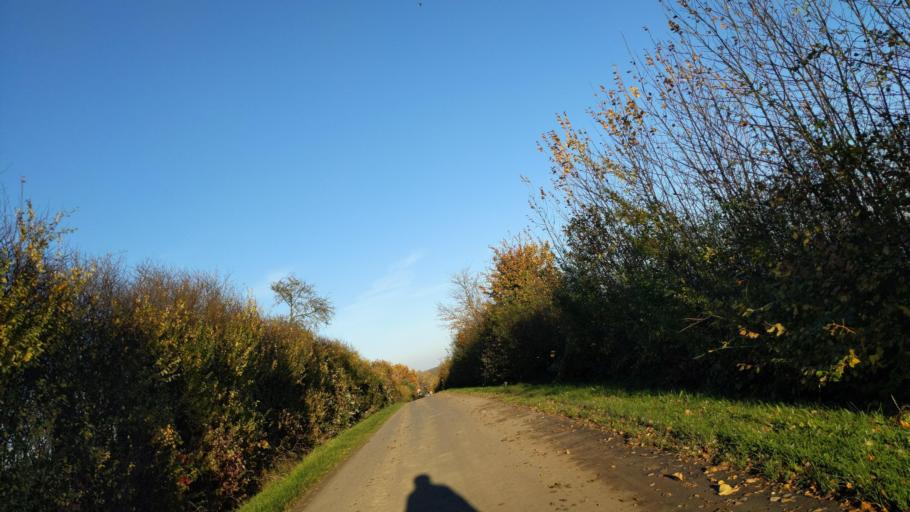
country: DE
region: Schleswig-Holstein
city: Gross Sarau
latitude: 53.7667
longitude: 10.7271
